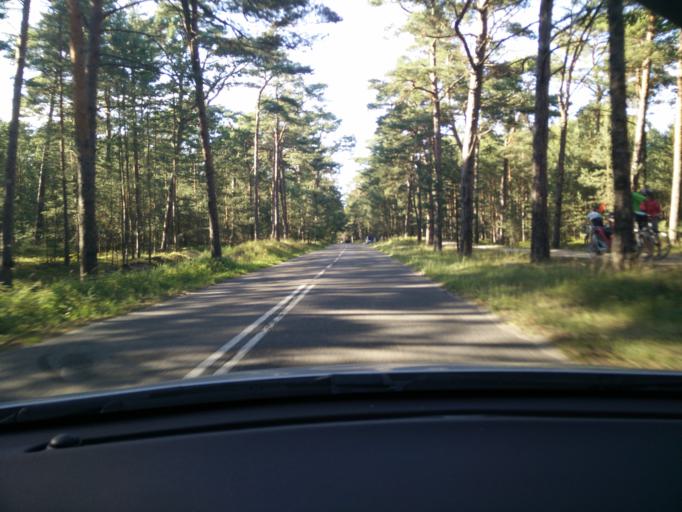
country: PL
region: Pomeranian Voivodeship
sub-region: Powiat pucki
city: Hel
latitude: 54.6451
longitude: 18.7699
